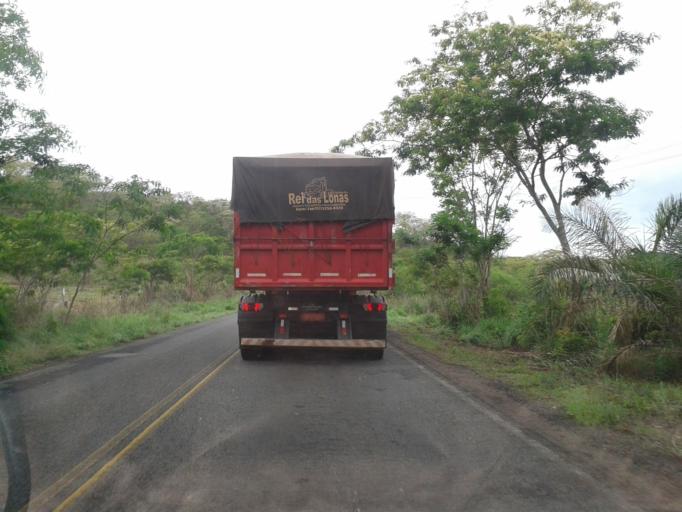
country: BR
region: Goias
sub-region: Caldas Novas
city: Caldas Novas
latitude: -18.0616
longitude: -48.6896
